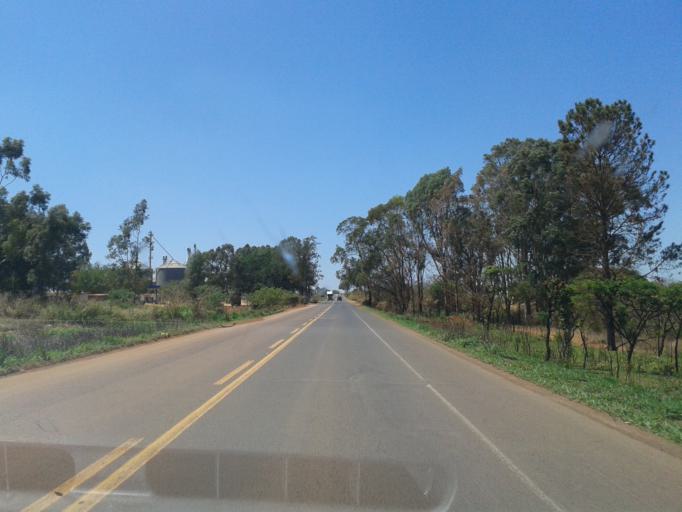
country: BR
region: Minas Gerais
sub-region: Araxa
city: Araxa
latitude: -19.4097
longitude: -47.3078
